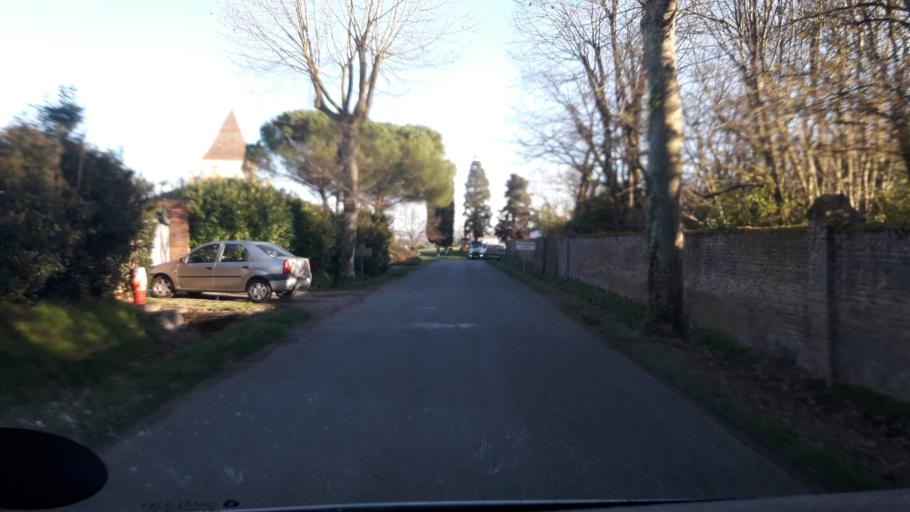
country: FR
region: Midi-Pyrenees
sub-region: Departement du Gers
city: Gimont
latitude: 43.6006
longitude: 0.9808
